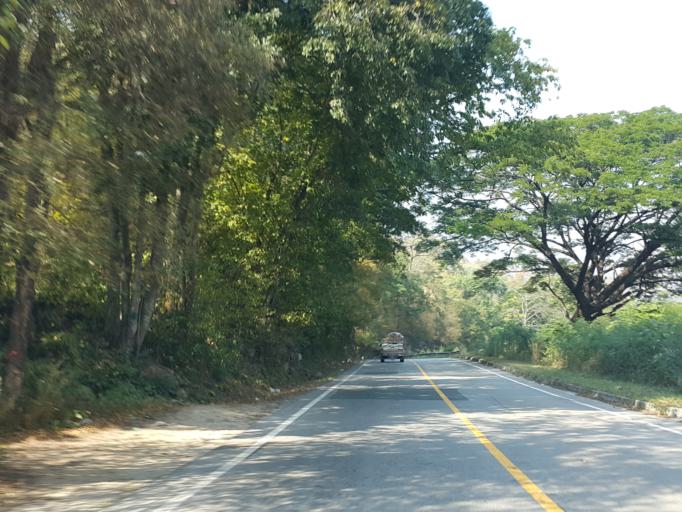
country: TH
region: Chiang Mai
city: Hot
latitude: 18.2280
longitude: 98.5620
